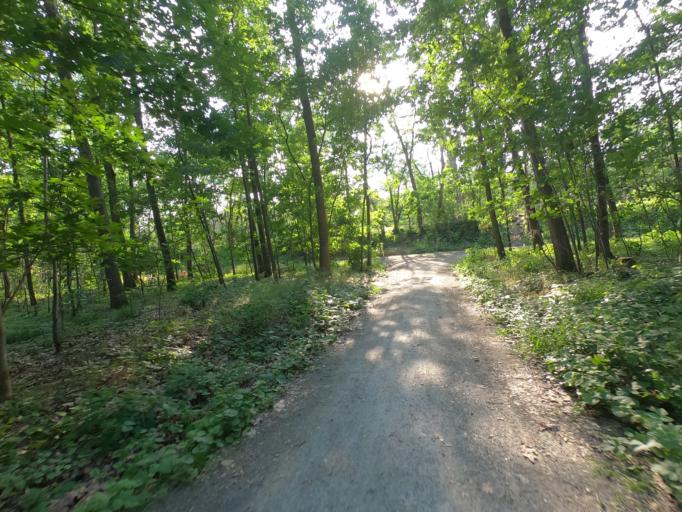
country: DE
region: Hesse
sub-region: Regierungsbezirk Darmstadt
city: Russelsheim
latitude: 49.9636
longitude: 8.4197
